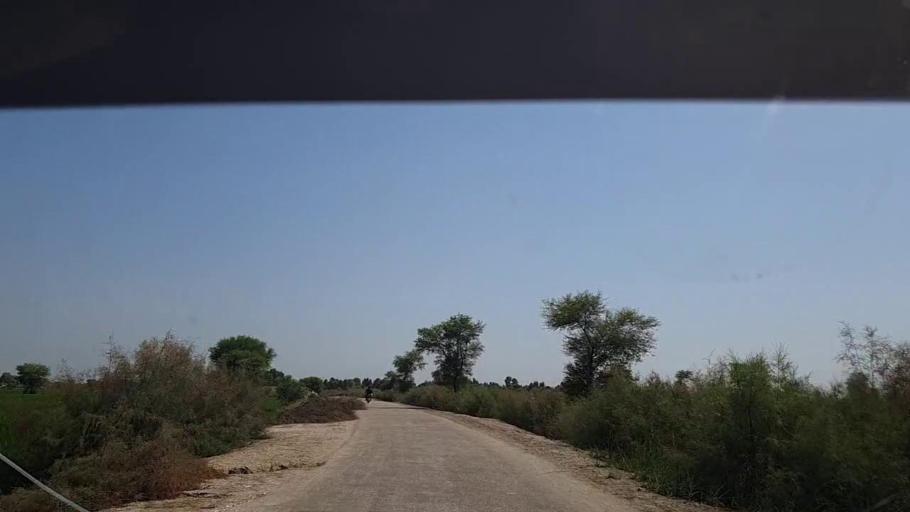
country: PK
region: Sindh
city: Kandhkot
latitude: 28.1676
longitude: 69.1604
